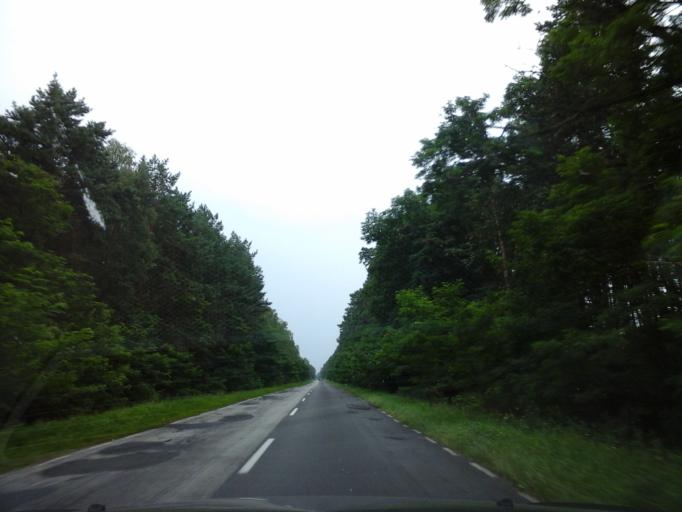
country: PL
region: Lubusz
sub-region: Powiat strzelecko-drezdenecki
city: Drezdenko
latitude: 52.7784
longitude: 15.8428
